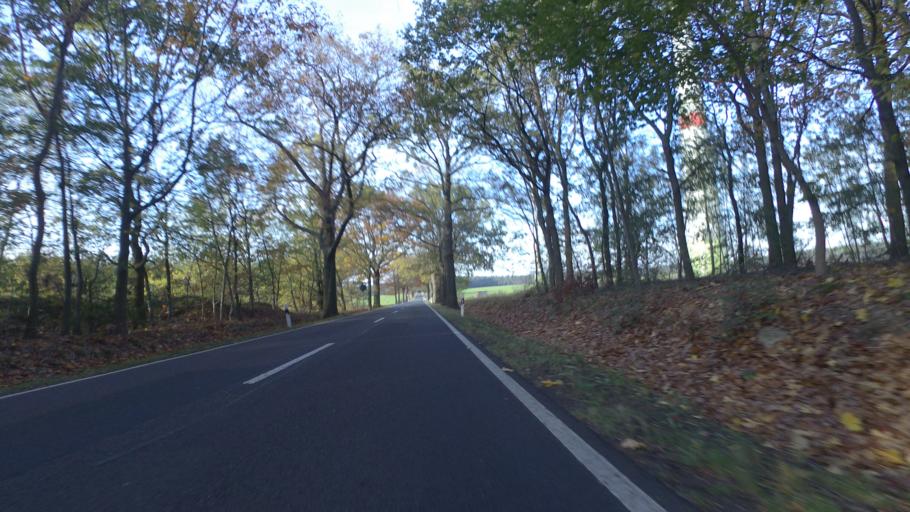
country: DE
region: Brandenburg
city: Trebbin
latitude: 52.2067
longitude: 13.3048
